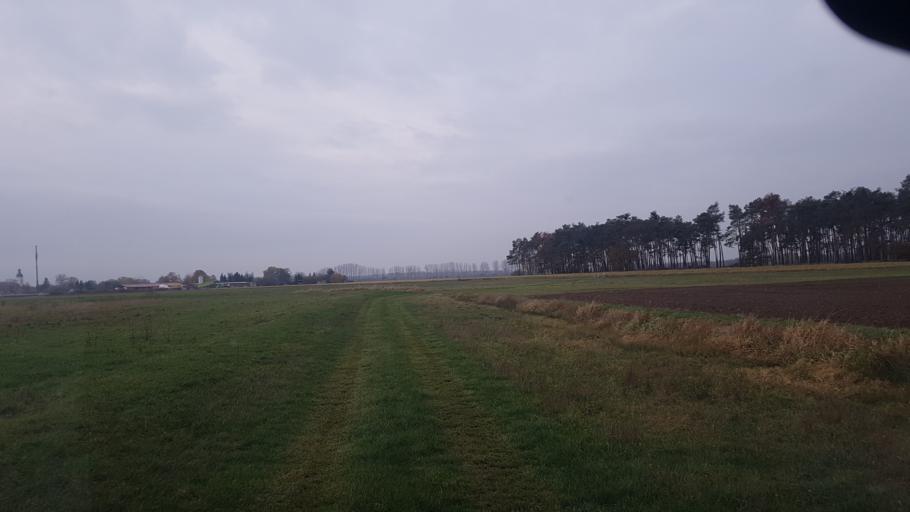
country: DE
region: Brandenburg
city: Falkenberg
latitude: 51.6038
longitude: 13.3030
